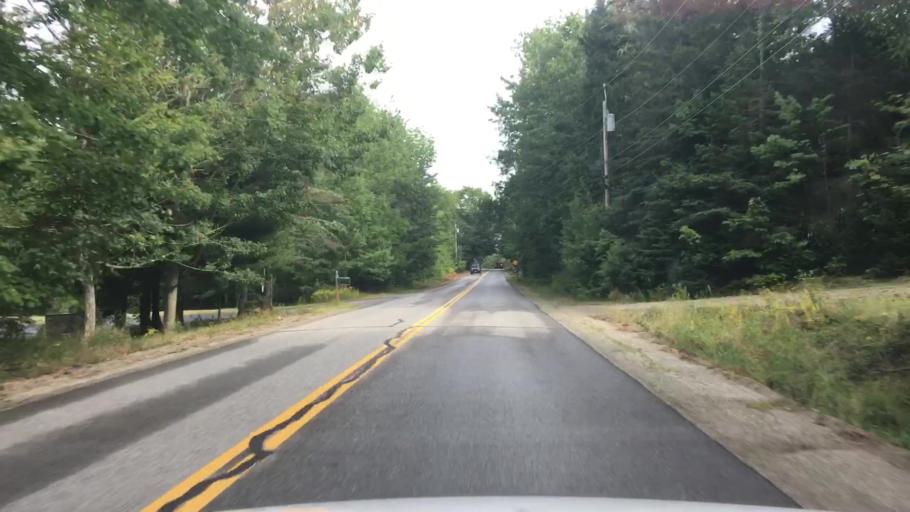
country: US
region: Maine
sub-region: Hancock County
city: Trenton
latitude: 44.4373
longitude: -68.4002
